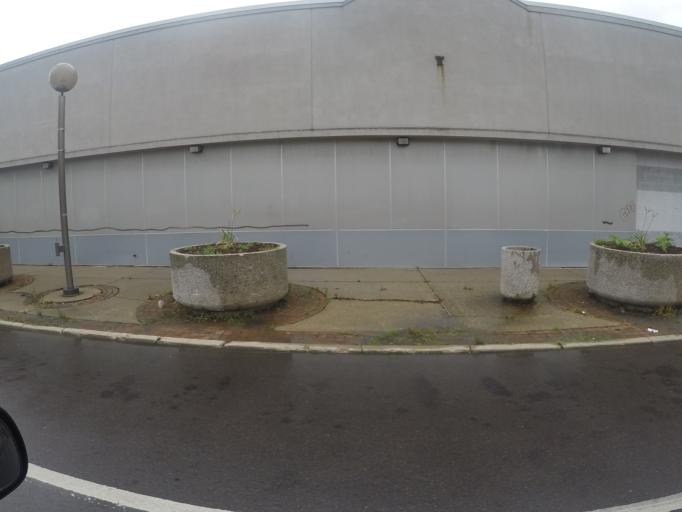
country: US
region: Michigan
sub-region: Wayne County
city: Grosse Pointe Park
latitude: 42.4029
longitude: -82.9382
